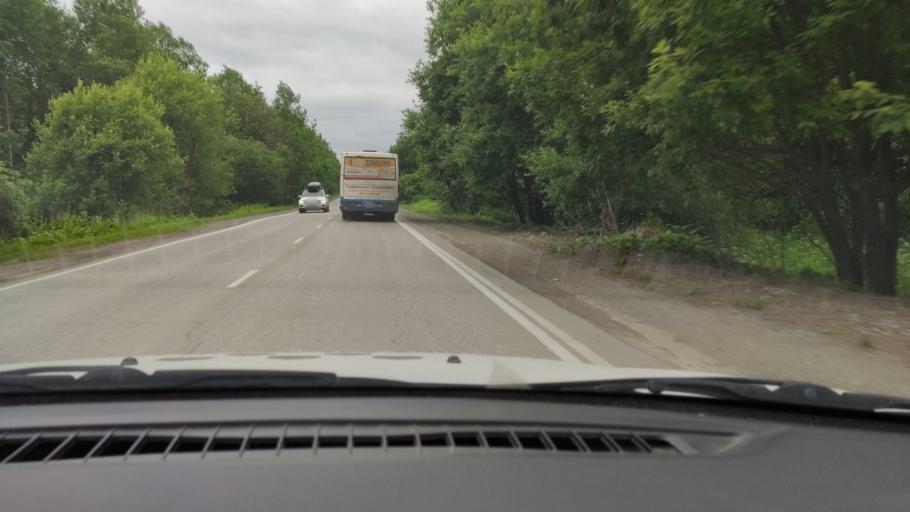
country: RU
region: Perm
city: Novyye Lyady
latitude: 58.0222
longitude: 56.6589
